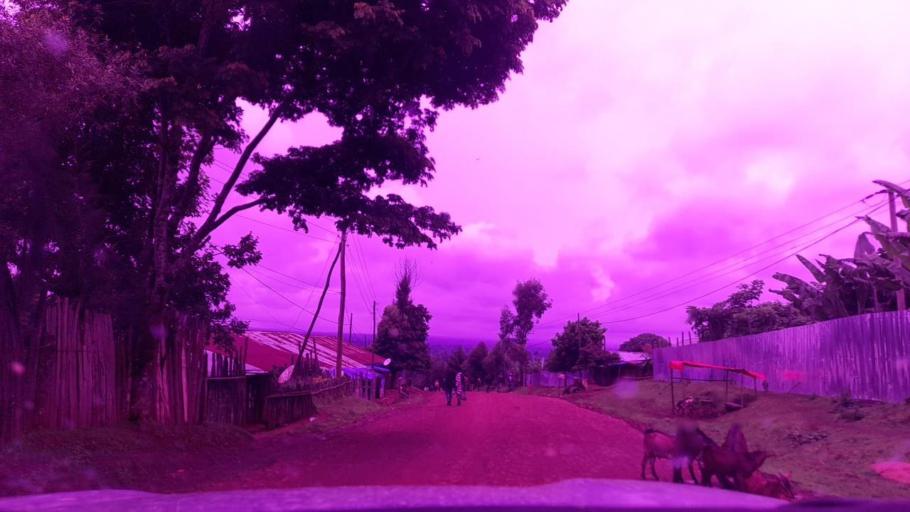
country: ET
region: Southern Nations, Nationalities, and People's Region
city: Tippi
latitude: 7.5932
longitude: 35.7509
